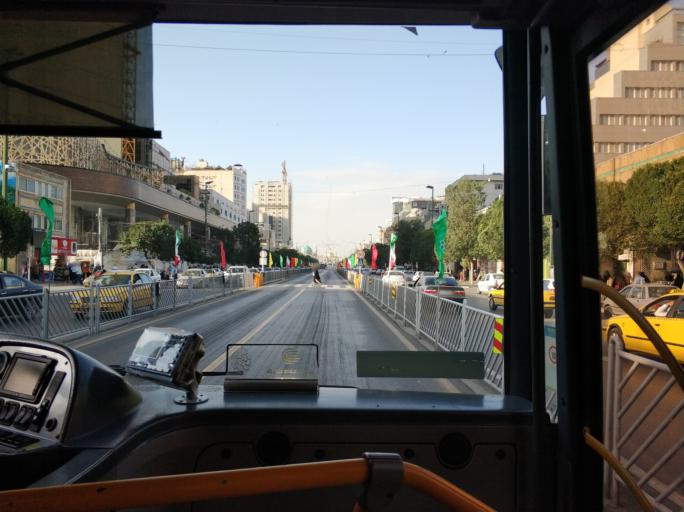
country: IR
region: Razavi Khorasan
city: Mashhad
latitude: 36.2801
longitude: 59.6090
